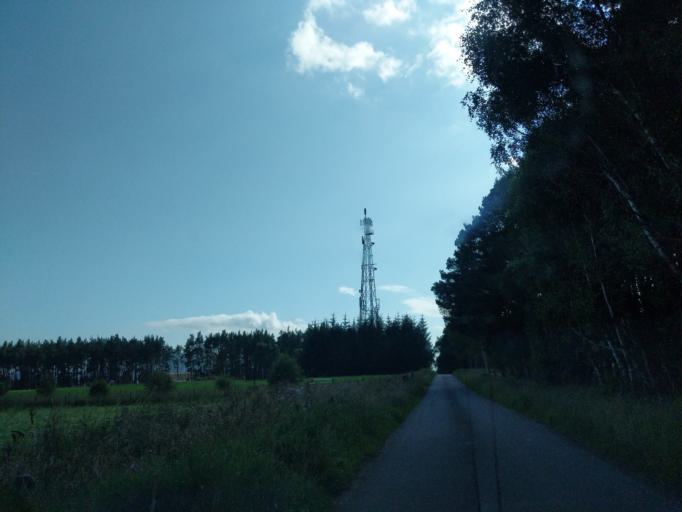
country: GB
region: Scotland
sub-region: Moray
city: Rothes
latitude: 57.4847
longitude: -3.2304
